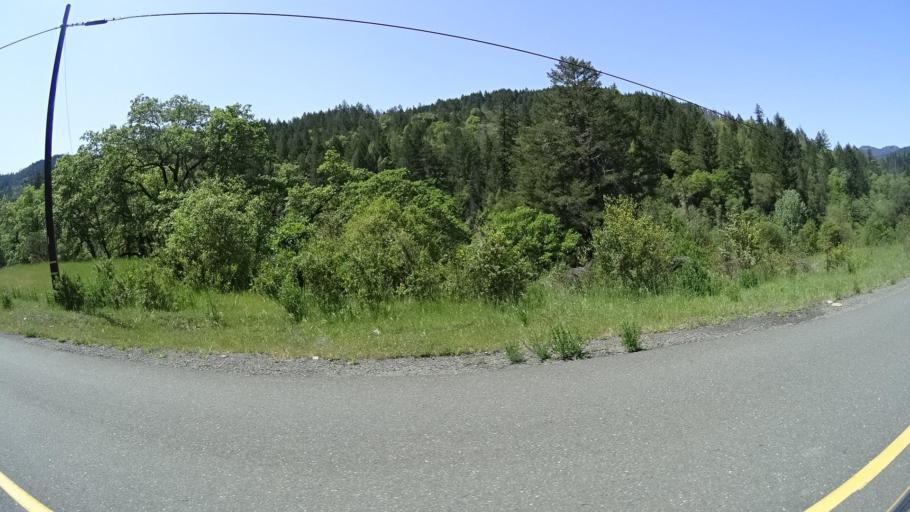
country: US
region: California
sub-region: Humboldt County
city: Redway
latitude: 40.2149
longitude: -123.5963
